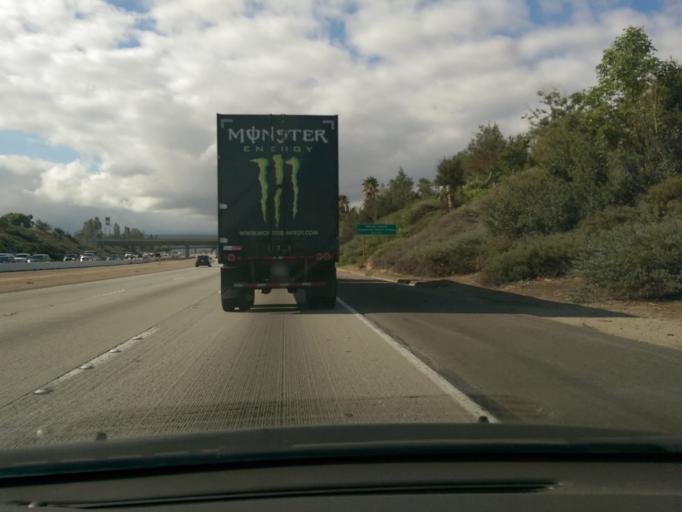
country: US
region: California
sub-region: Riverside County
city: Norco
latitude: 33.9449
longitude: -117.5554
